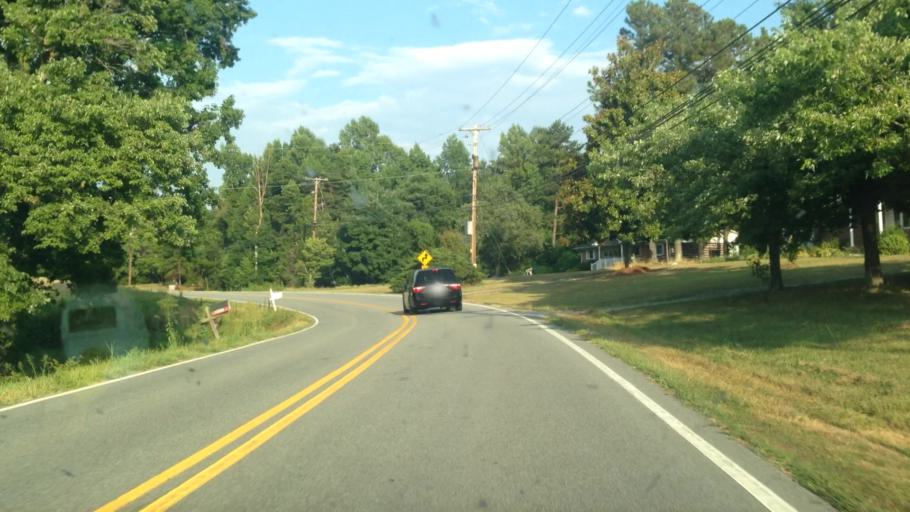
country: US
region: North Carolina
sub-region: Davidson County
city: Thomasville
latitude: 35.9398
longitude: -80.0682
